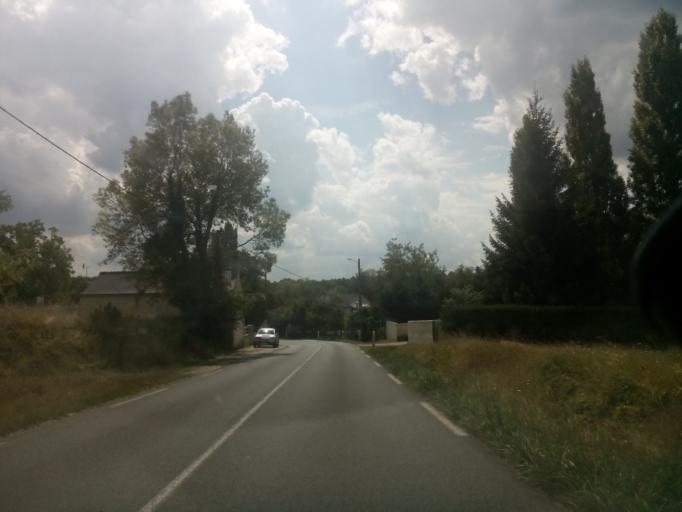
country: FR
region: Centre
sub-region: Departement d'Indre-et-Loire
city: Cheille
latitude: 47.2728
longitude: 0.4242
